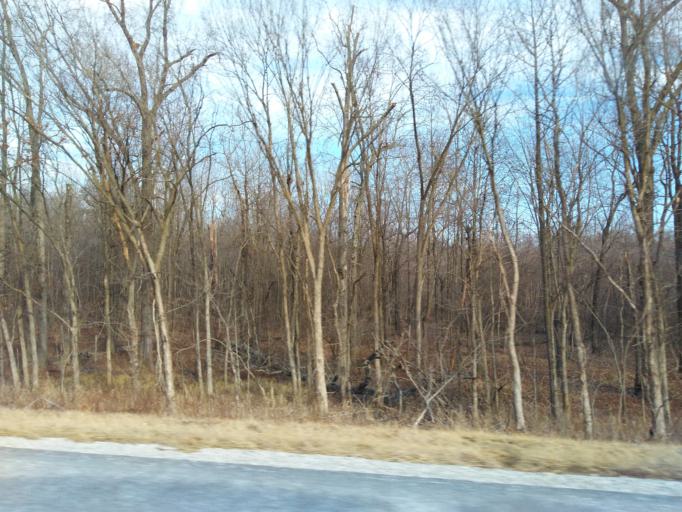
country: US
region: Illinois
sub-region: Jefferson County
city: Mount Vernon
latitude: 38.2446
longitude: -88.9060
